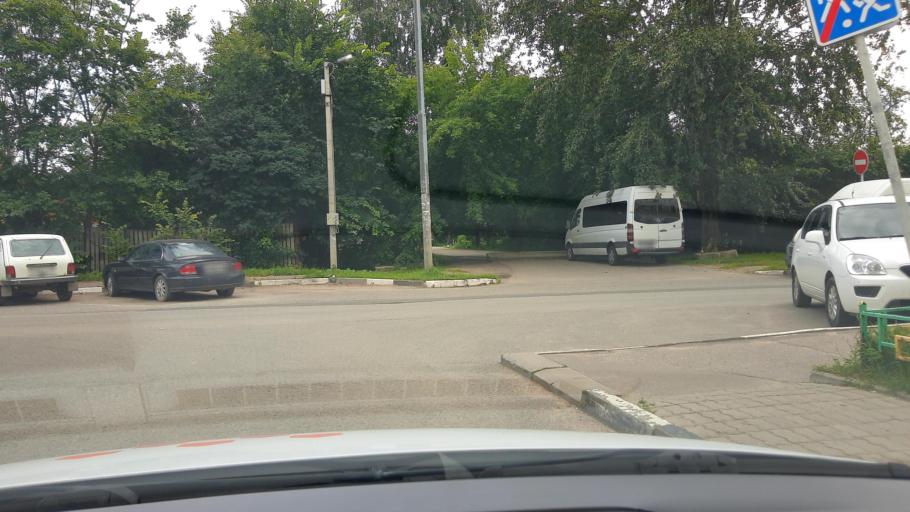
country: RU
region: Moskovskaya
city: Zheleznodorozhnyy
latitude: 55.7431
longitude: 37.9855
